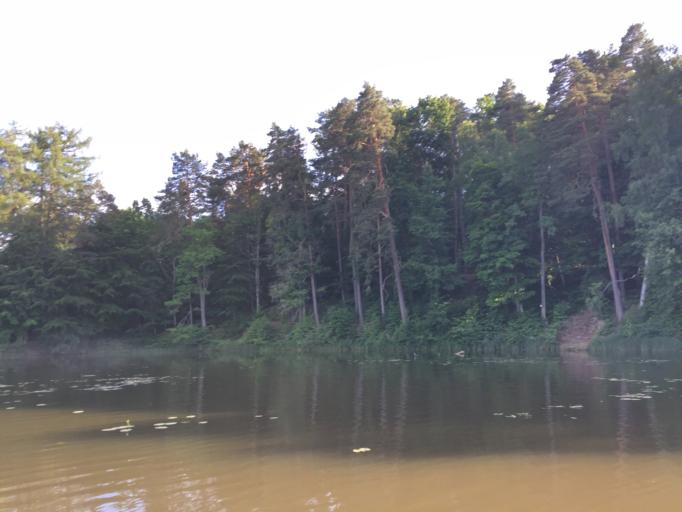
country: LV
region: Aizpute
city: Aizpute
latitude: 56.7269
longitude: 21.7356
